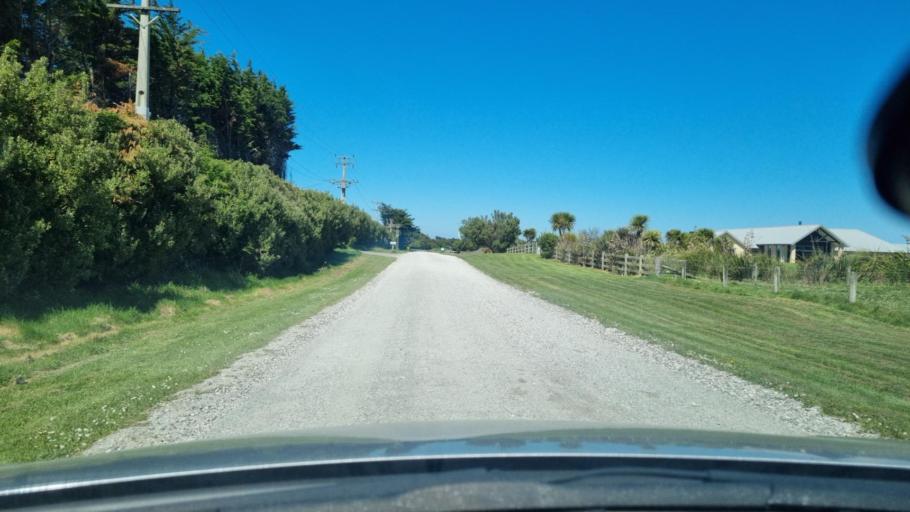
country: NZ
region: Southland
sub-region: Invercargill City
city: Invercargill
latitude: -46.4426
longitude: 168.2784
